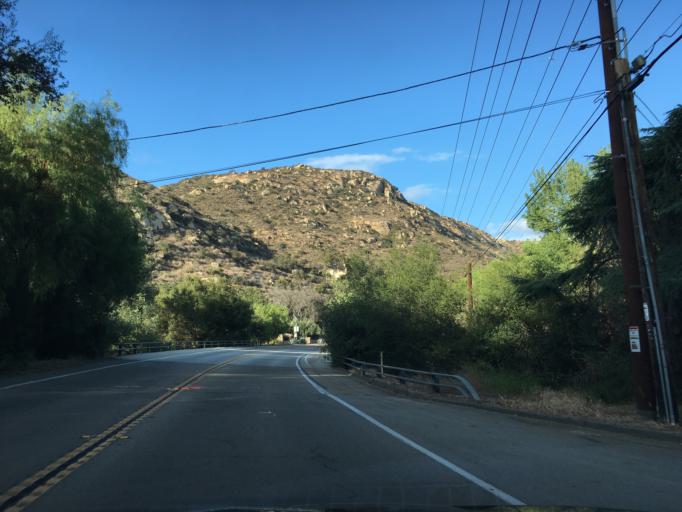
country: US
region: California
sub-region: San Diego County
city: Hidden Meadows
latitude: 33.2509
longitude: -117.1349
